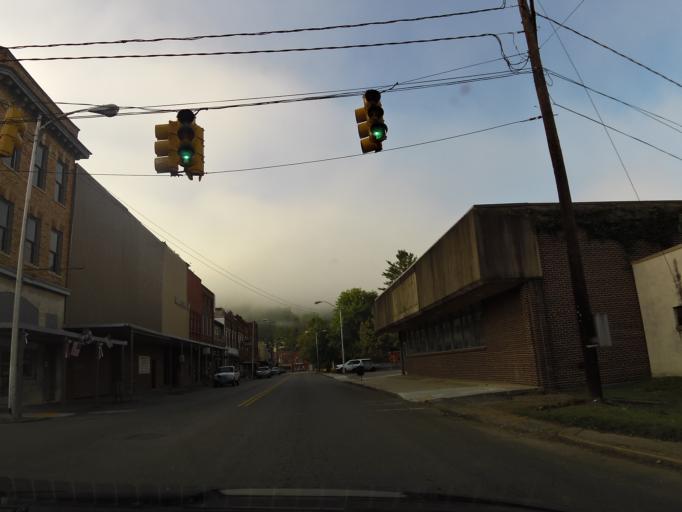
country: US
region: Tennessee
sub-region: Campbell County
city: Jellico
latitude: 36.5897
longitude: -84.1266
